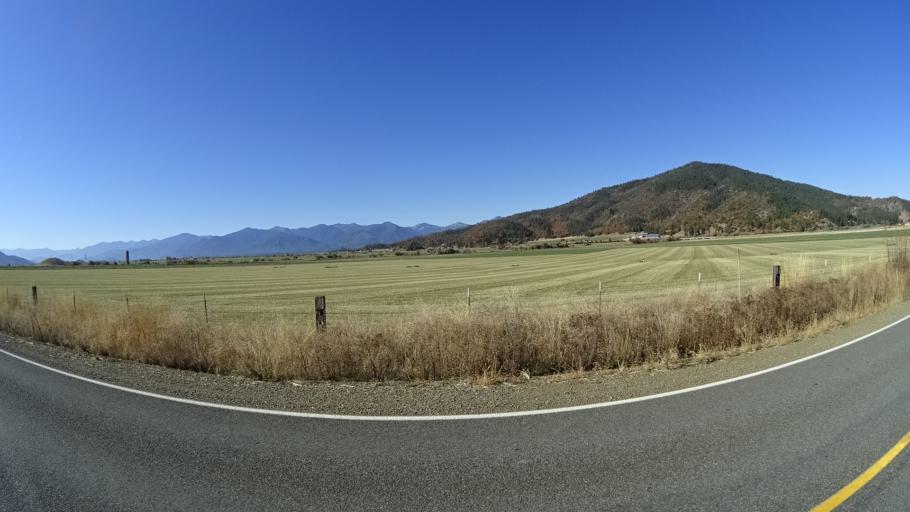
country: US
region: California
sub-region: Siskiyou County
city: Yreka
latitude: 41.5956
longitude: -122.8419
